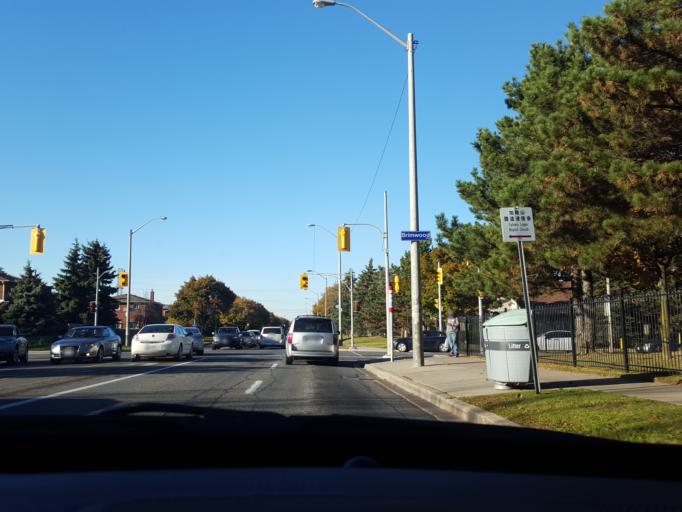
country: CA
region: Ontario
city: Scarborough
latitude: 43.8107
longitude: -79.2795
